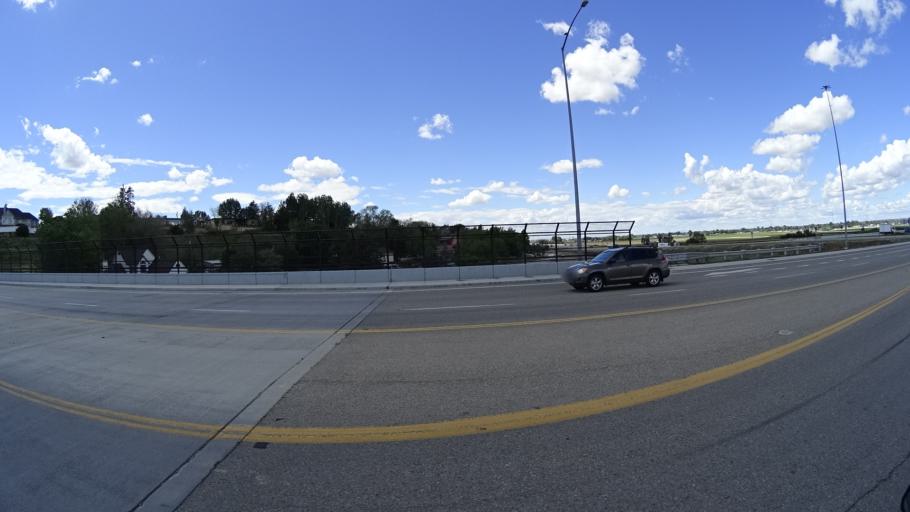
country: US
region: Idaho
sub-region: Ada County
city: Meridian
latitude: 43.5919
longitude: -116.4338
